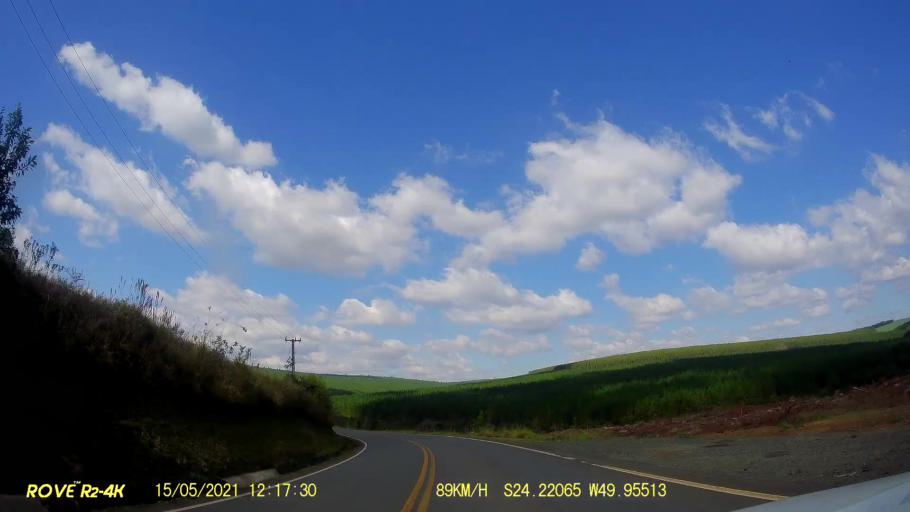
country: BR
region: Parana
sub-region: Jaguariaiva
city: Jaguariaiva
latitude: -24.2201
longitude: -49.9555
